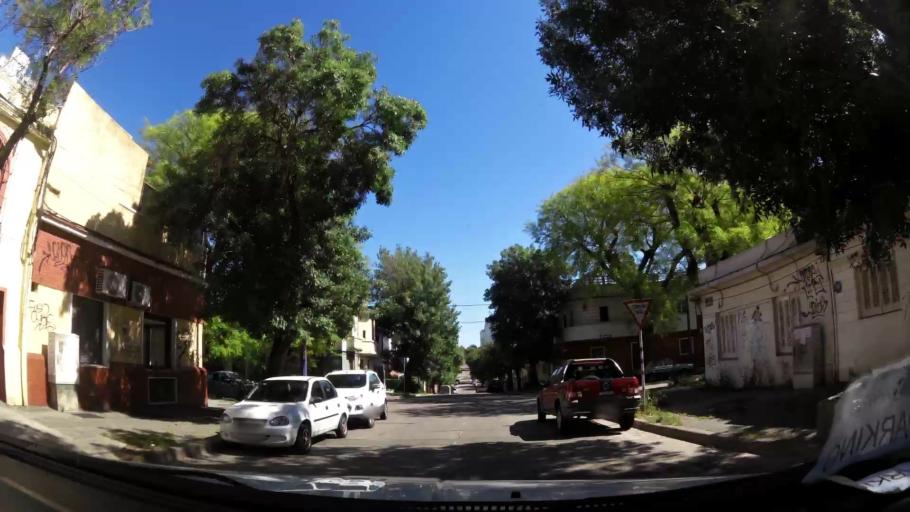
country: UY
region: Montevideo
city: Montevideo
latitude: -34.9188
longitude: -56.1636
